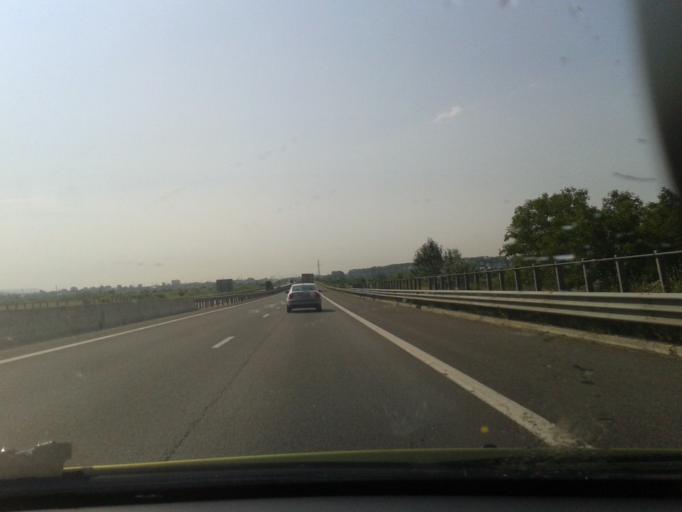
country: RO
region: Arges
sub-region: Comuna Maracineni
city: Maracineni
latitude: 44.8848
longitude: 24.8563
